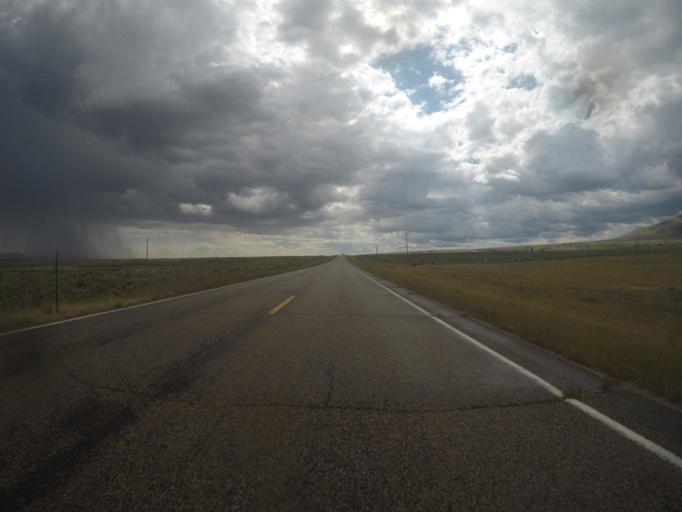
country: US
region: Utah
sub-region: Daggett County
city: Manila
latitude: 41.0227
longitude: -109.9053
